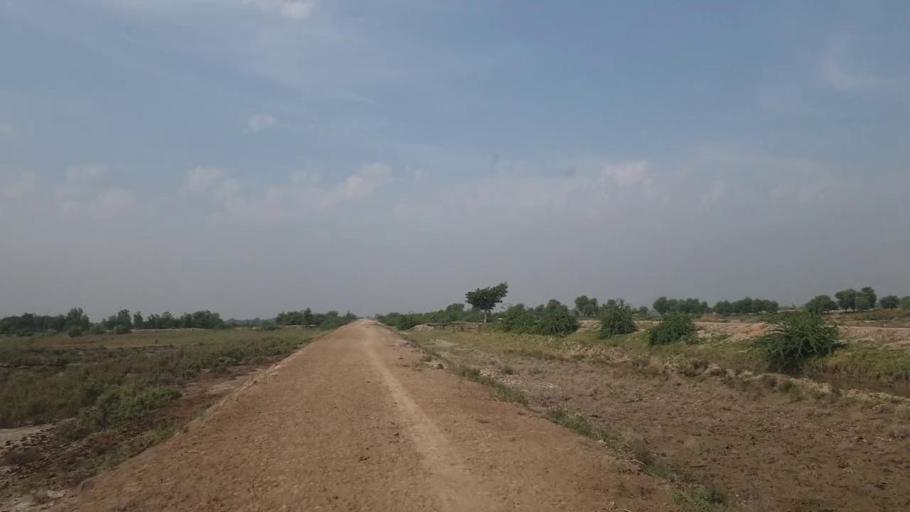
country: PK
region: Sindh
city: Rajo Khanani
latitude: 24.9599
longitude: 69.0233
